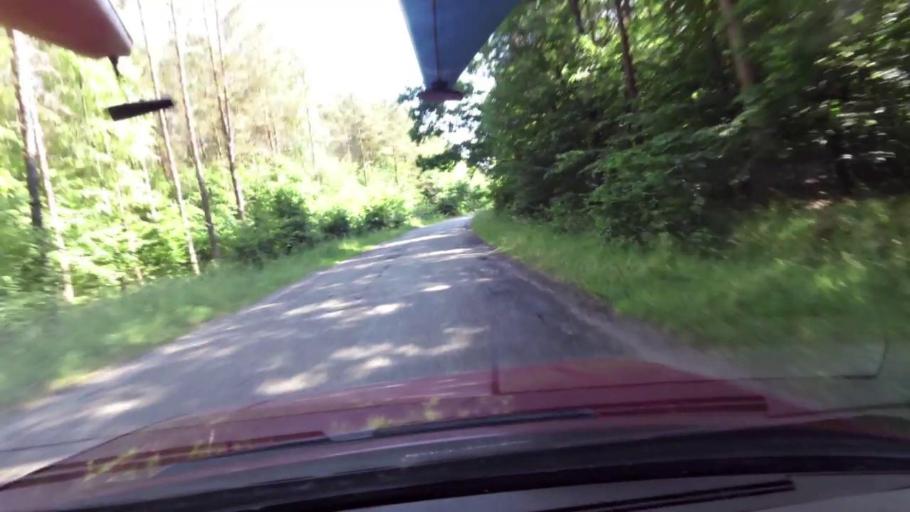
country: PL
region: Pomeranian Voivodeship
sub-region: Powiat slupski
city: Kepice
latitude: 54.1557
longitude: 16.9091
